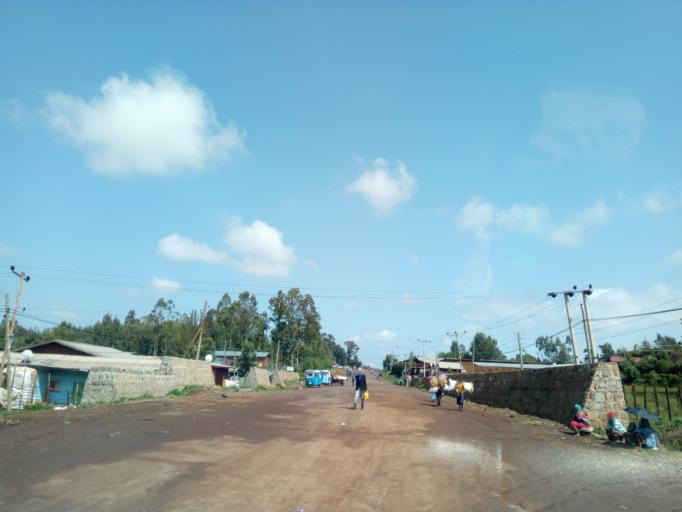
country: ET
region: Oromiya
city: Waliso
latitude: 8.5447
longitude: 37.9665
